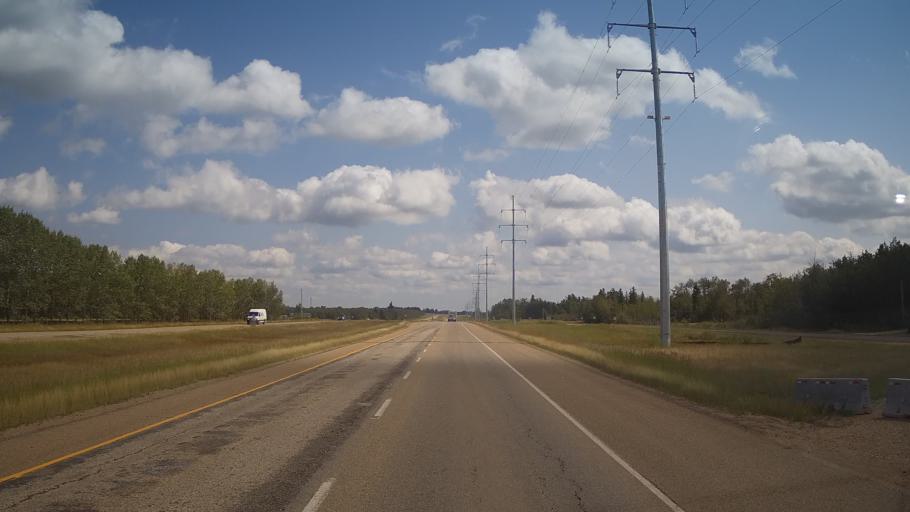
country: CA
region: Alberta
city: Sherwood Park
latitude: 53.4431
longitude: -113.2264
